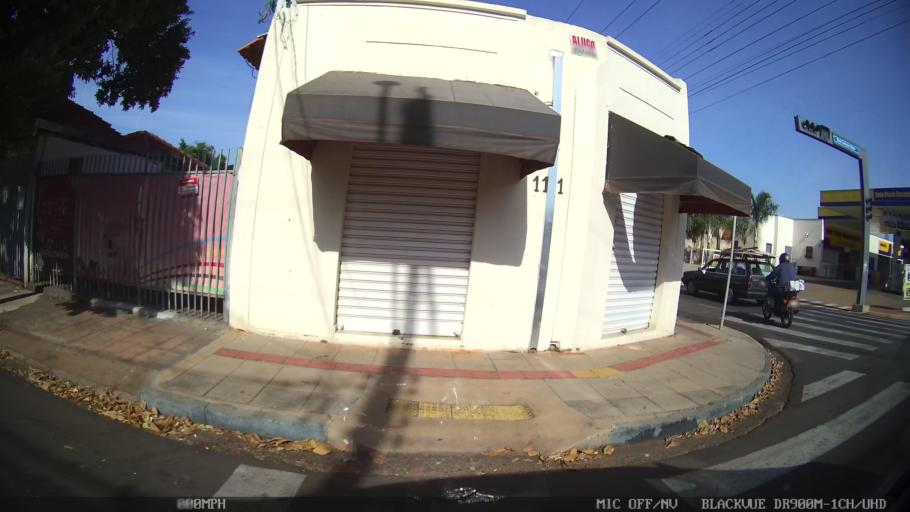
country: BR
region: Sao Paulo
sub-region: Sao Jose Do Rio Preto
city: Sao Jose do Rio Preto
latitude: -20.7999
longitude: -49.3861
